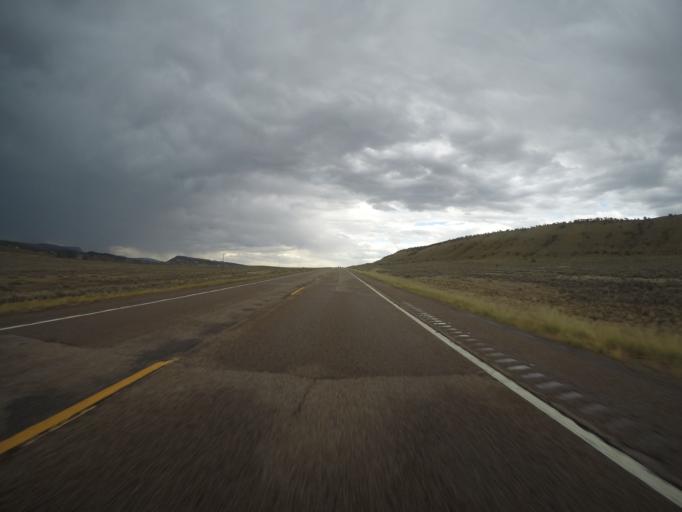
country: US
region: Colorado
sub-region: Rio Blanco County
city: Rangely
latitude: 40.2514
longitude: -108.8261
